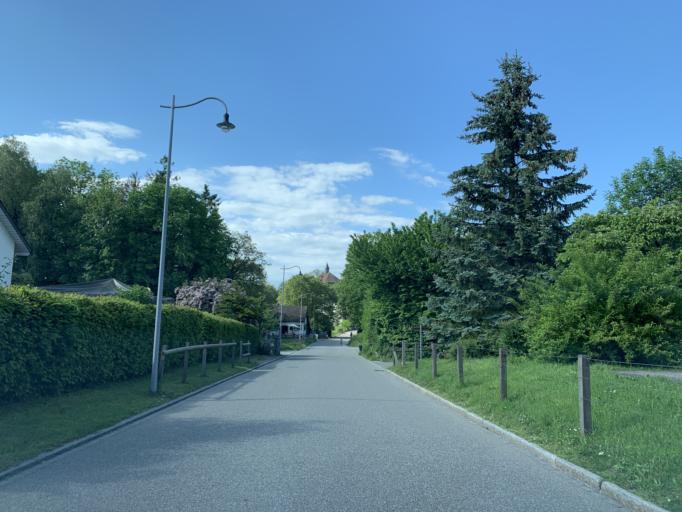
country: CH
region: Zurich
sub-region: Bezirk Winterthur
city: Kollbrunn / Kollbrunn (Dorfkern)
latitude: 47.4546
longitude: 8.7434
